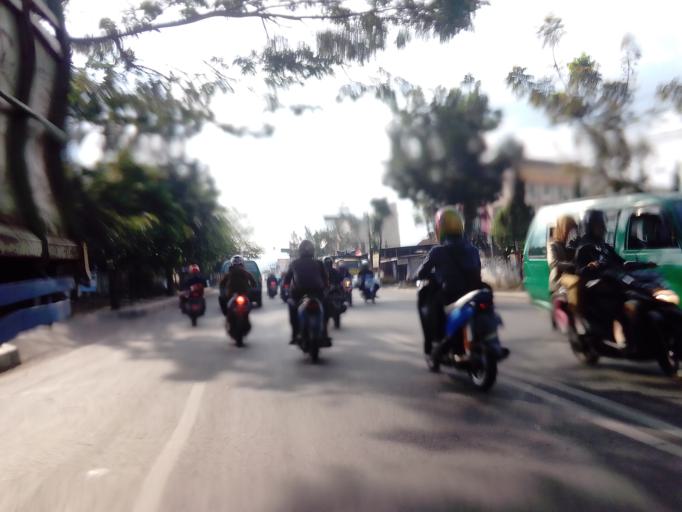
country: ID
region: West Java
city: Cileunyi
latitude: -6.9207
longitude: 107.7091
